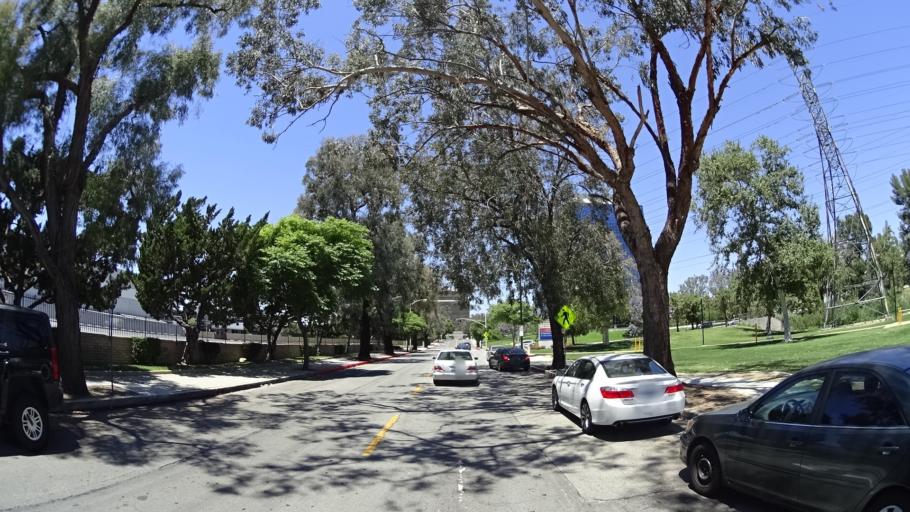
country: US
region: California
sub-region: Los Angeles County
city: Universal City
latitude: 34.1543
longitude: -118.3310
